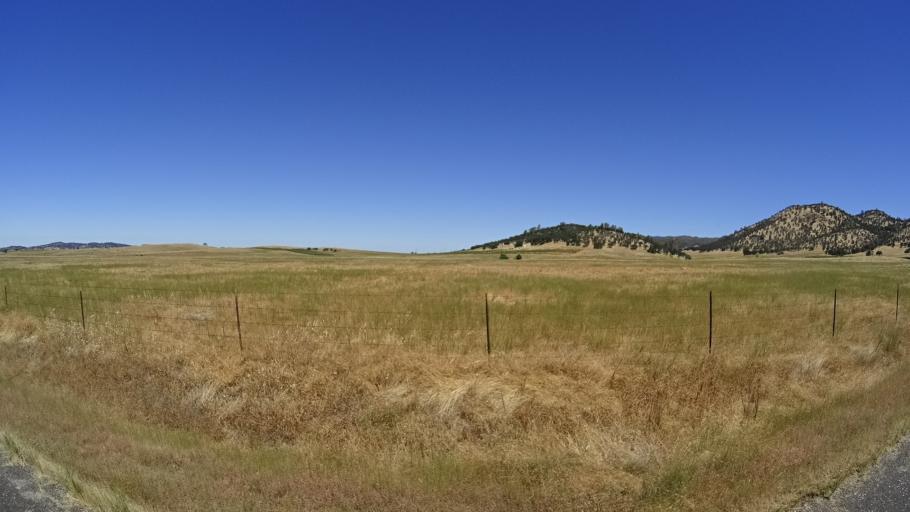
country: US
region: California
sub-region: Calaveras County
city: Copperopolis
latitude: 38.0416
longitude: -120.6974
